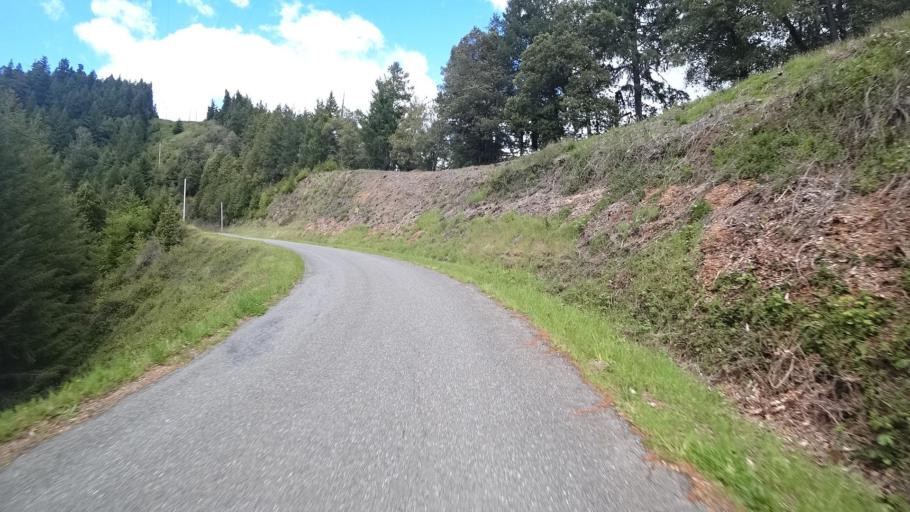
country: US
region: California
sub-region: Humboldt County
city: Blue Lake
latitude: 40.7626
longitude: -123.9214
